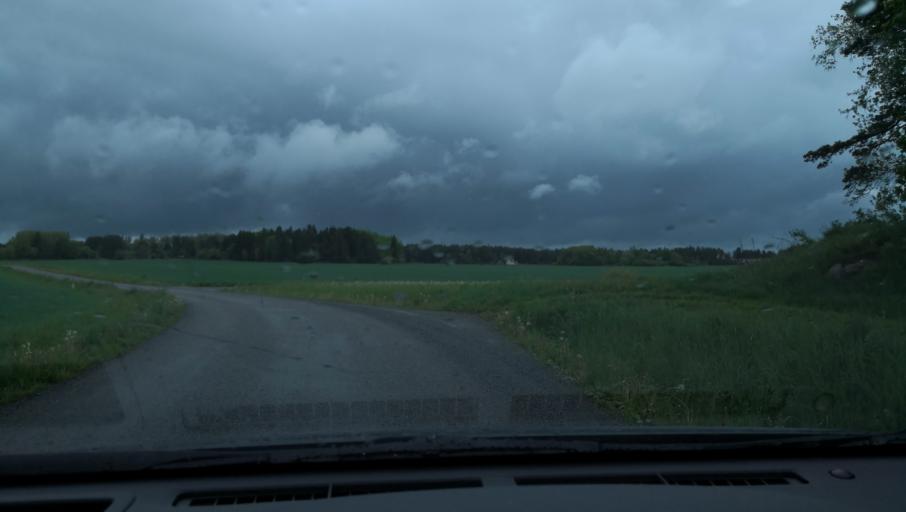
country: SE
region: Uppsala
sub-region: Enkopings Kommun
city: Orsundsbro
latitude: 59.8021
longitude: 17.3776
